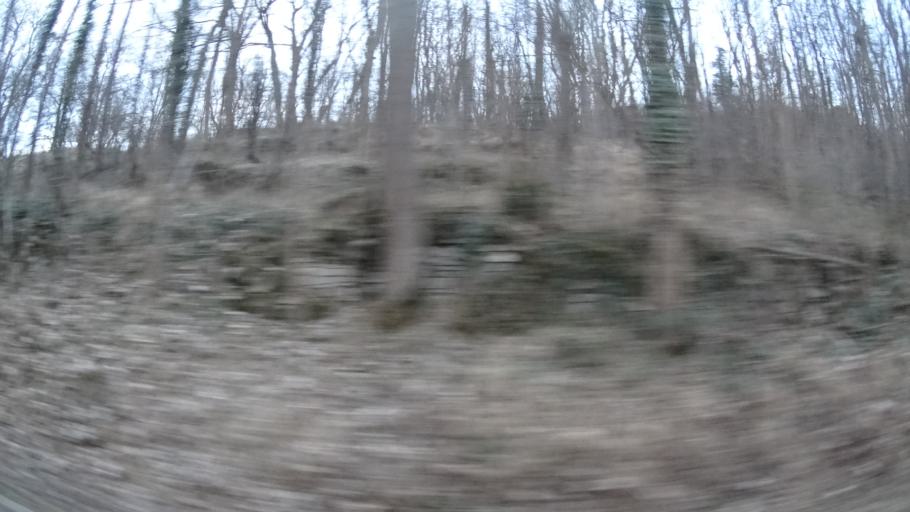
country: DE
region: Baden-Wuerttemberg
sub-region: Regierungsbezirk Stuttgart
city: Markgroningen
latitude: 48.9067
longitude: 9.0648
